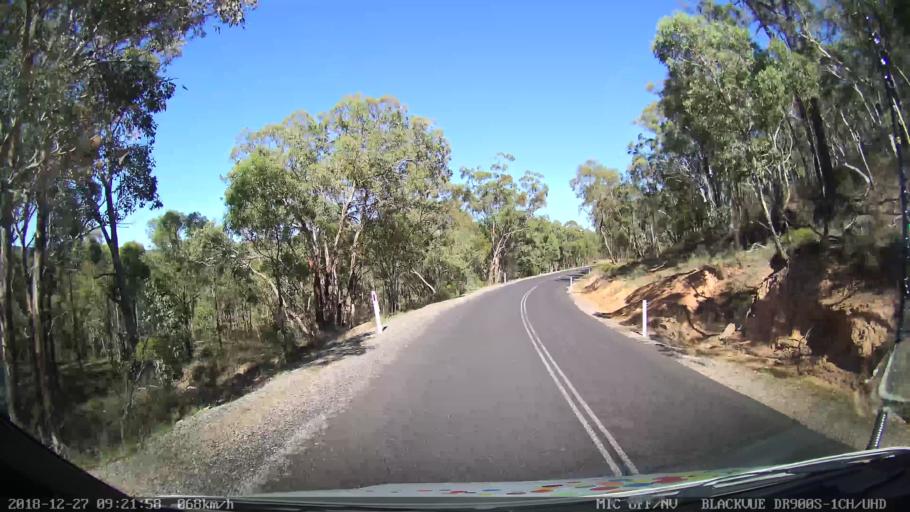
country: AU
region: New South Wales
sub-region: Lithgow
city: Portland
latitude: -33.1282
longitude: 150.0130
